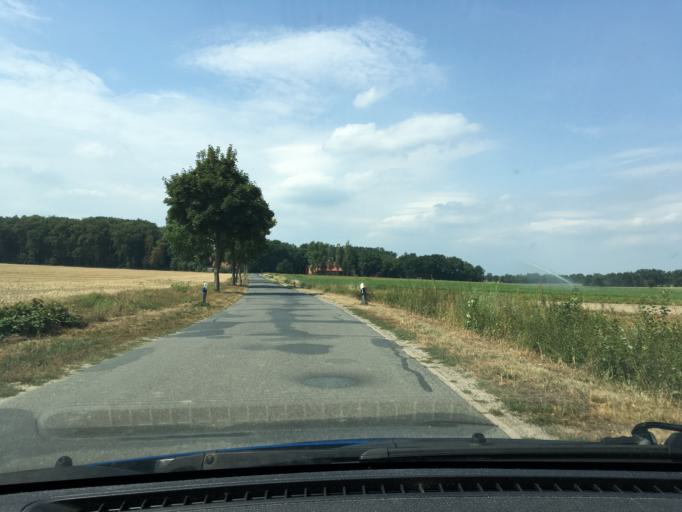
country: DE
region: Lower Saxony
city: Natendorf
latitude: 53.1159
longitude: 10.4416
